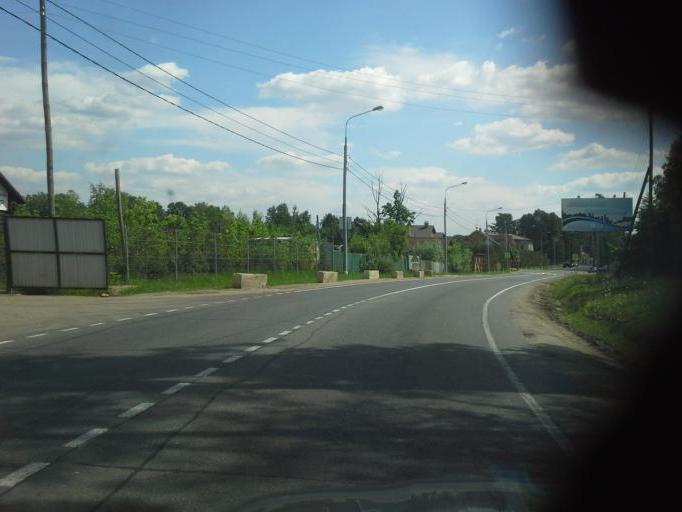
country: RU
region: Moskovskaya
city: Barvikha
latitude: 55.7170
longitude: 37.2681
